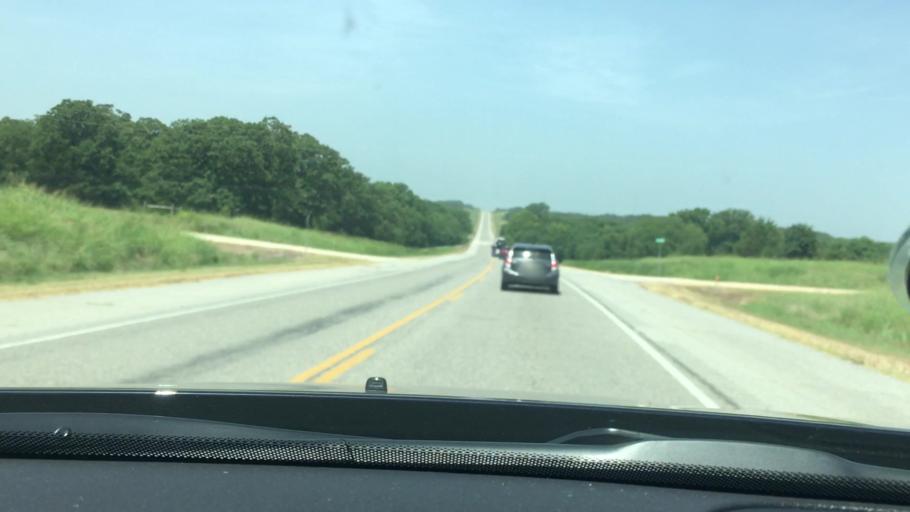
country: US
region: Oklahoma
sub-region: Coal County
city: Coalgate
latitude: 34.6109
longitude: -96.3887
